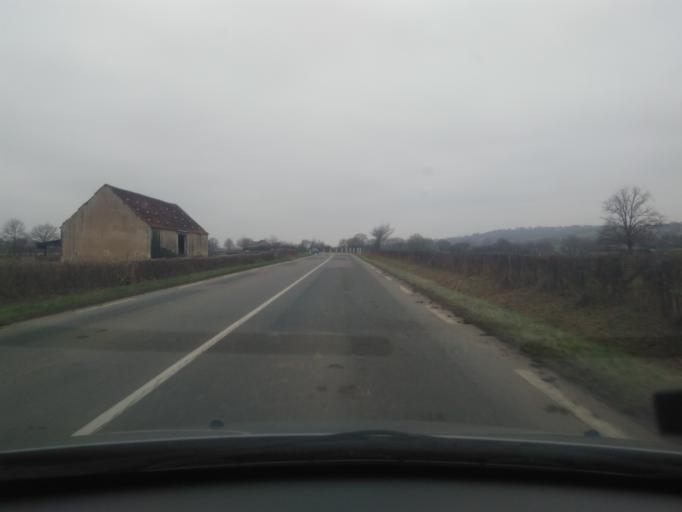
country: FR
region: Centre
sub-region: Departement du Cher
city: Charenton-du-Cher
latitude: 46.7310
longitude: 2.5887
